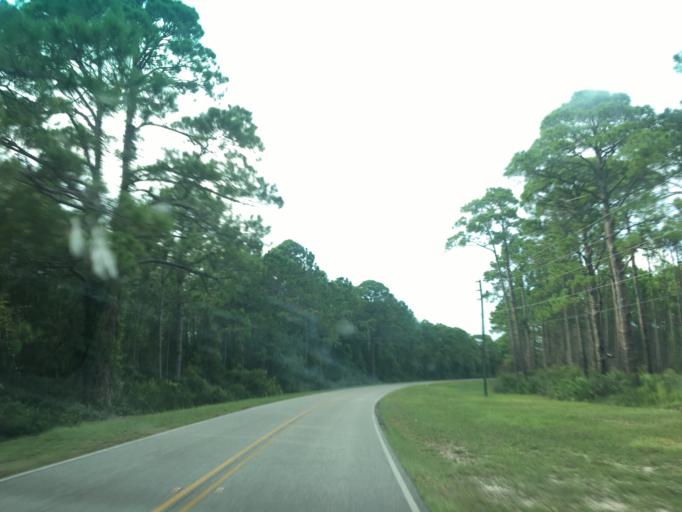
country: US
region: Florida
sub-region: Wakulla County
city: Crawfordville
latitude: 29.9284
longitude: -84.3780
